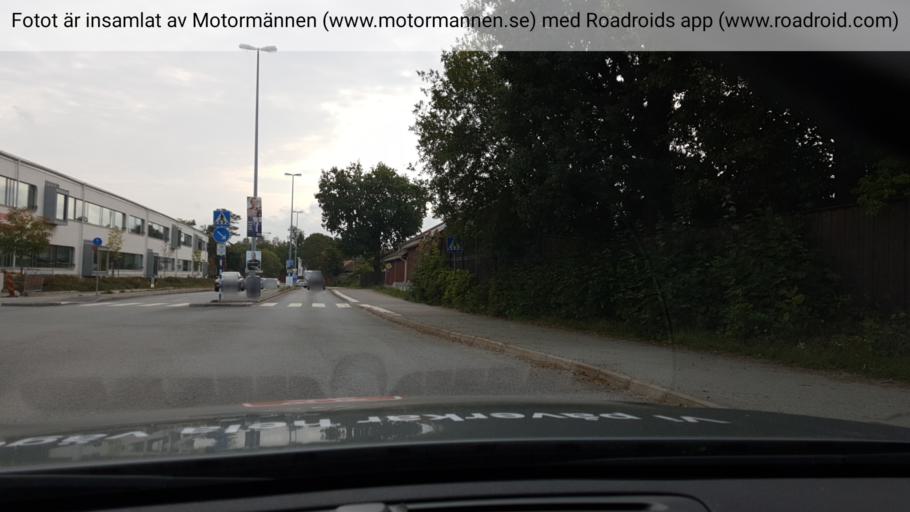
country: SE
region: Stockholm
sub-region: Huddinge Kommun
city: Segeltorp
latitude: 59.2789
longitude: 17.9432
